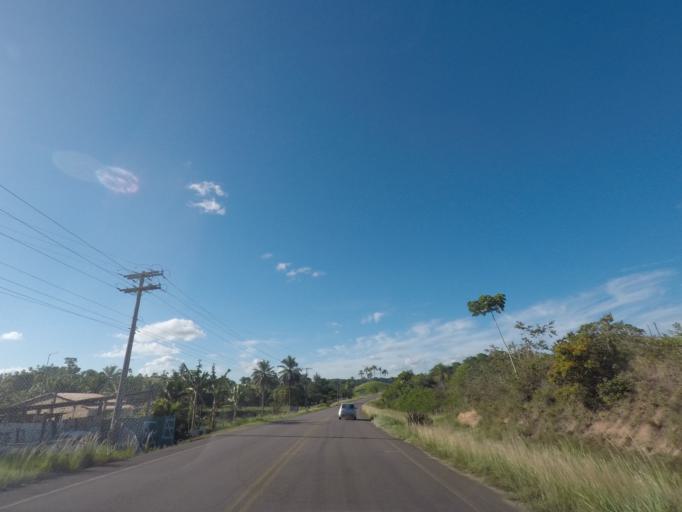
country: BR
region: Bahia
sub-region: Nazare
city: Nazare
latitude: -13.0711
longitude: -39.0028
